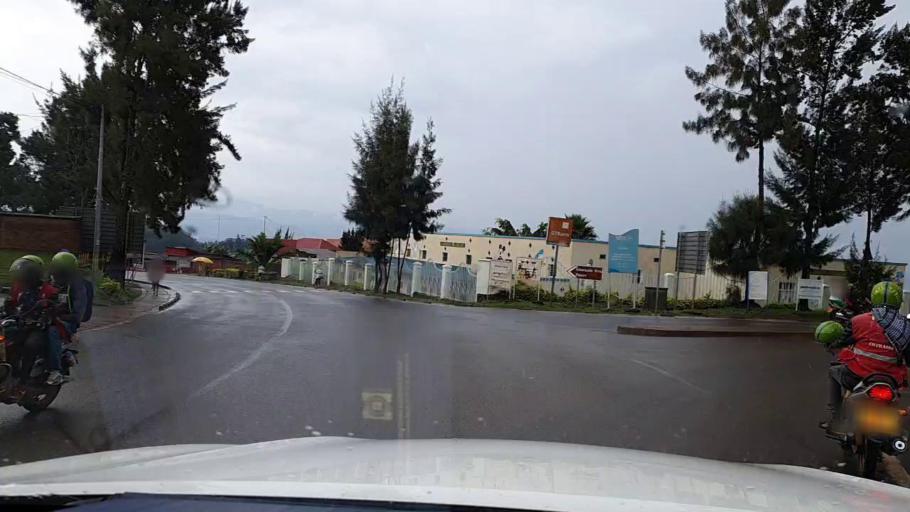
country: RW
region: Western Province
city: Cyangugu
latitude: -2.4848
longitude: 28.9132
